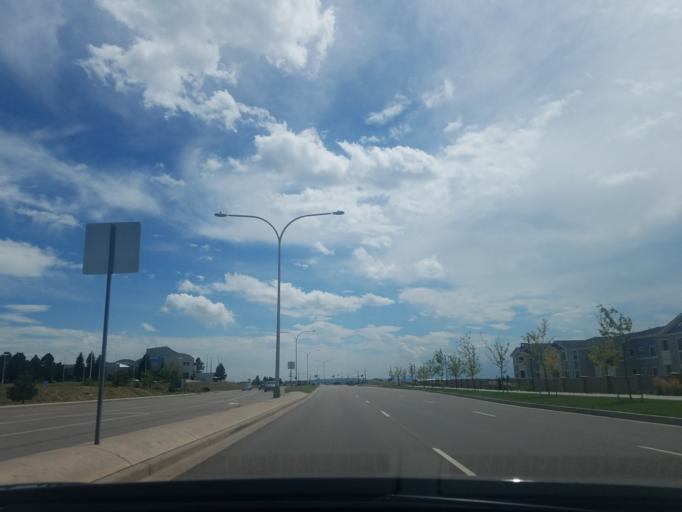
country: US
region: Colorado
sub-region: El Paso County
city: Gleneagle
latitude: 38.9941
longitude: -104.7981
